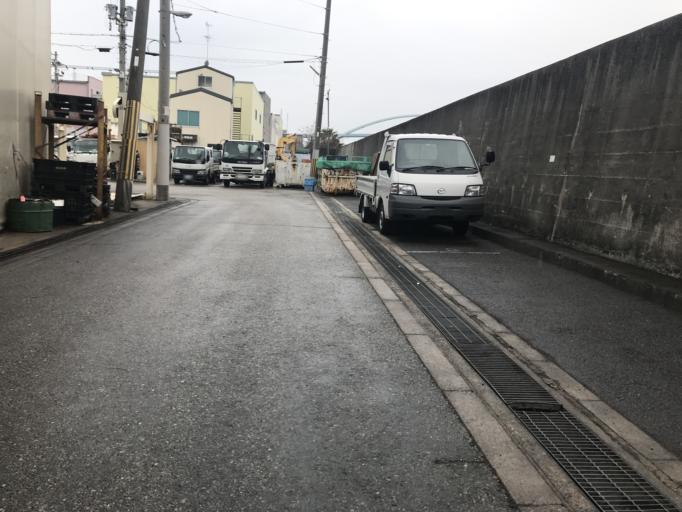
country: JP
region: Osaka
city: Sakai
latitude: 34.6263
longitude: 135.4712
